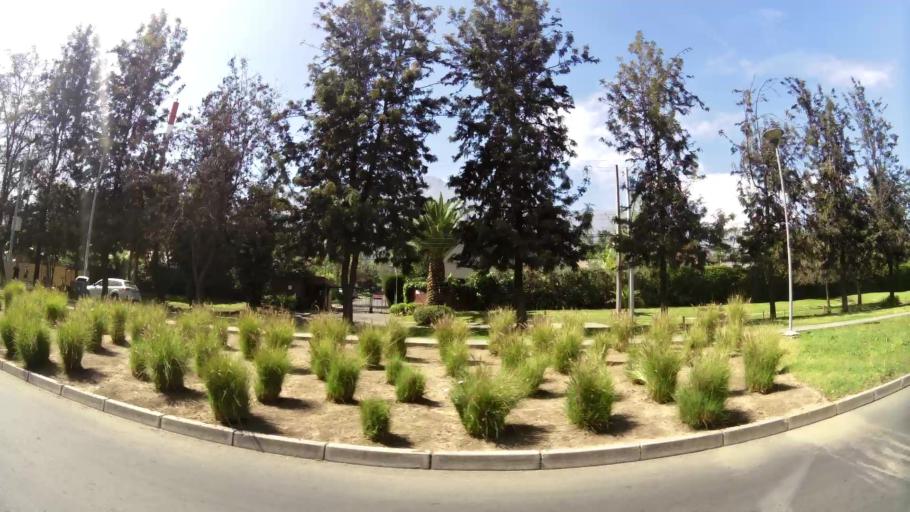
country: CL
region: Santiago Metropolitan
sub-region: Provincia de Santiago
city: Villa Presidente Frei, Nunoa, Santiago, Chile
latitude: -33.4539
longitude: -70.5288
